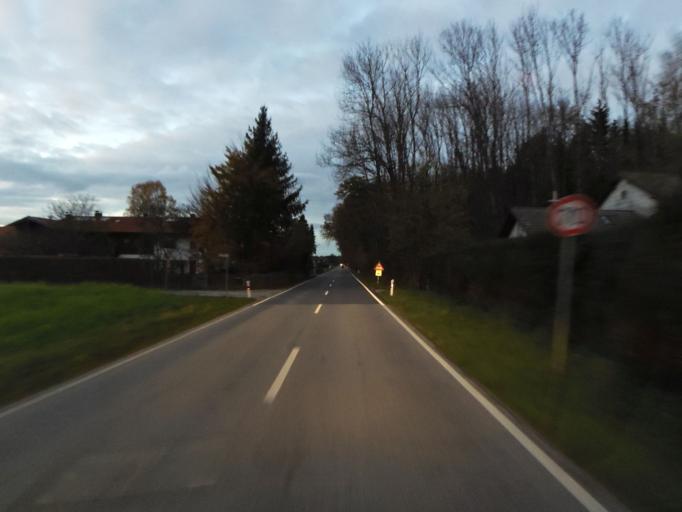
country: DE
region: Bavaria
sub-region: Upper Bavaria
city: Valley
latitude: 47.9239
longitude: 11.7562
